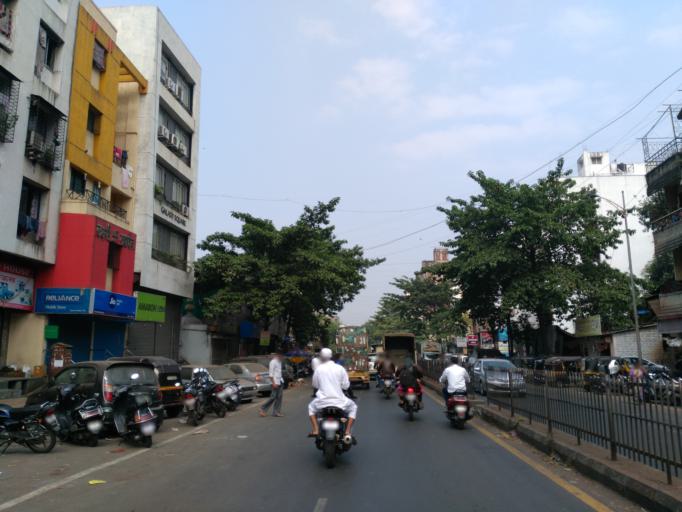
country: IN
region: Maharashtra
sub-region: Pune Division
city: Pune
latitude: 18.5158
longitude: 73.8686
